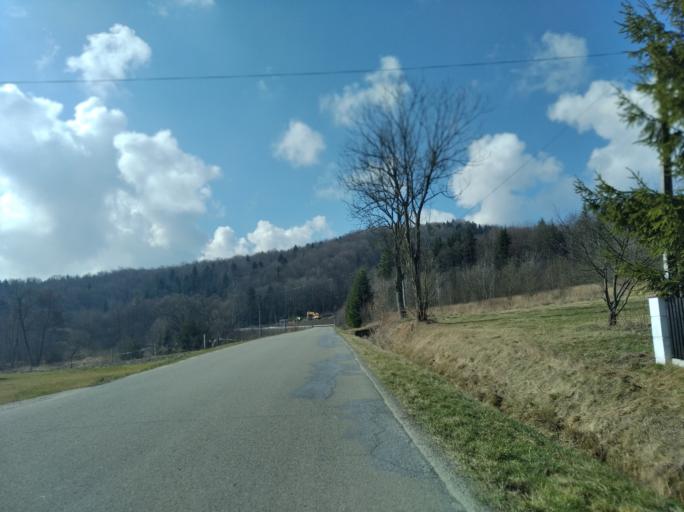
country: PL
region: Subcarpathian Voivodeship
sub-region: Powiat strzyzowski
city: Frysztak
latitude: 49.8720
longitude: 21.5617
